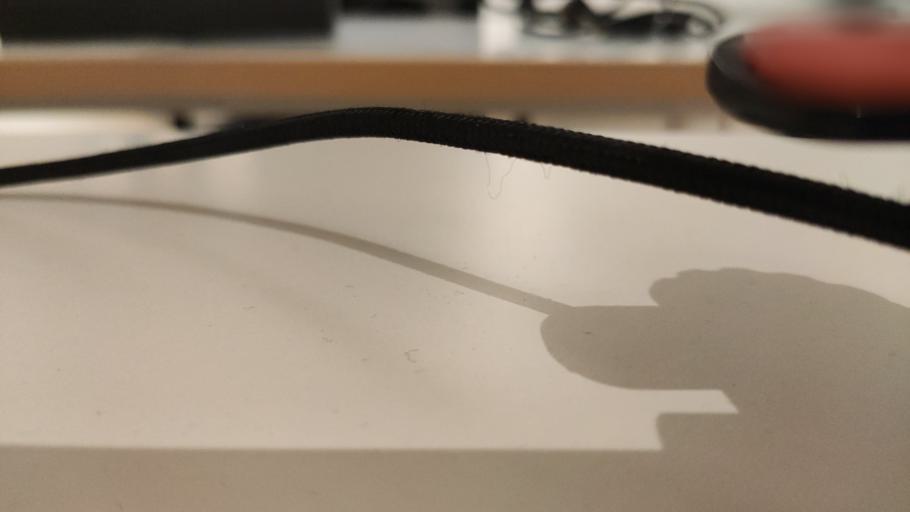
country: RU
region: Moskovskaya
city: Dorokhovo
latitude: 55.4119
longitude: 36.3705
